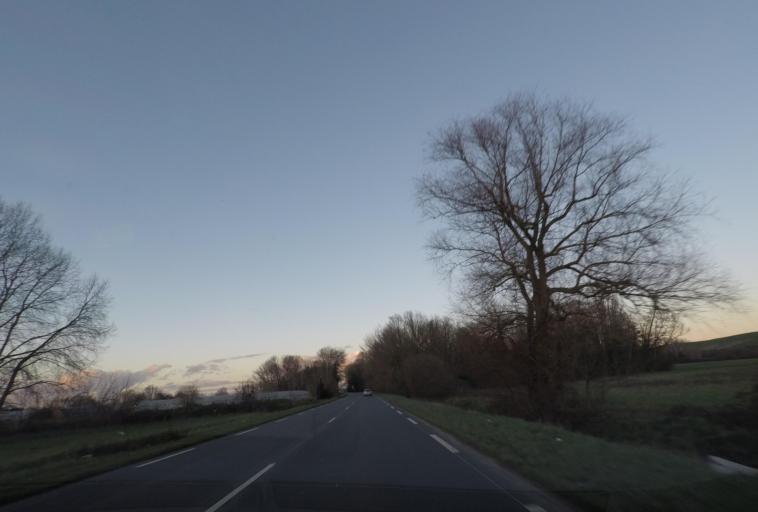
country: FR
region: Ile-de-France
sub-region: Departement de l'Essonne
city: Vert-le-Grand
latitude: 48.5803
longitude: 2.3668
